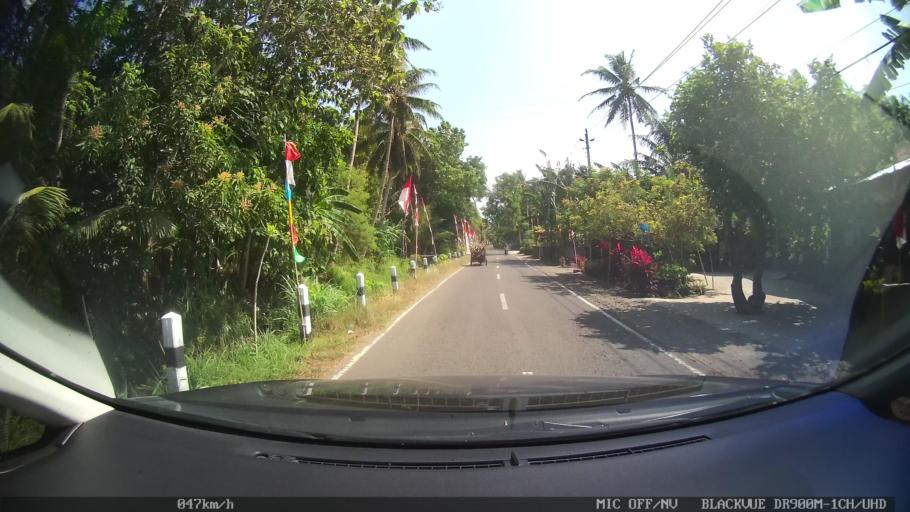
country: ID
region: Daerah Istimewa Yogyakarta
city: Srandakan
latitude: -7.9171
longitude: 110.1548
